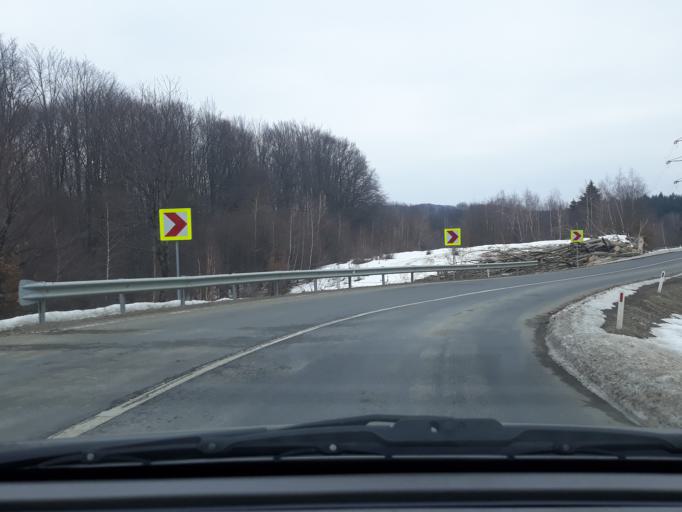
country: RO
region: Bihor
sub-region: Oras Alesd
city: Padurea Neagra
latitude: 47.1215
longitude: 22.4366
